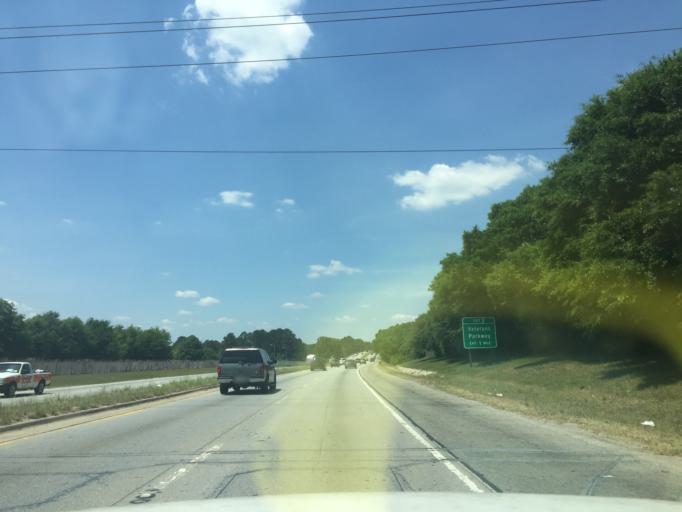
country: US
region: Georgia
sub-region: Chatham County
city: Savannah
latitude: 32.0332
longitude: -81.1273
